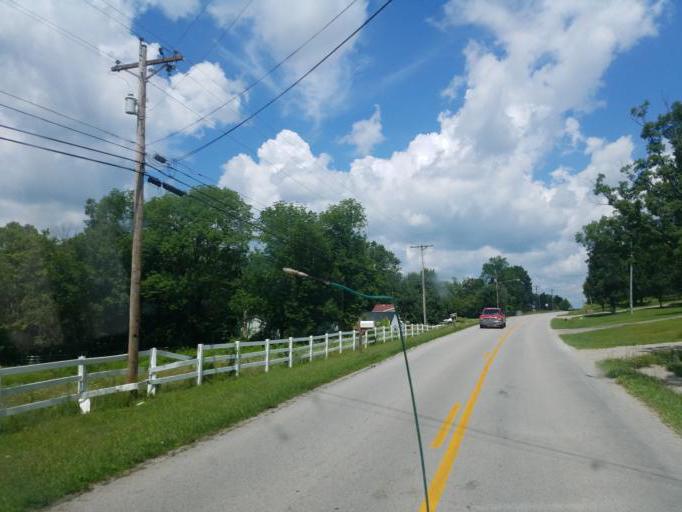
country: US
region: Kentucky
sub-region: Grayson County
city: Leitchfield
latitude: 37.5001
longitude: -86.3098
